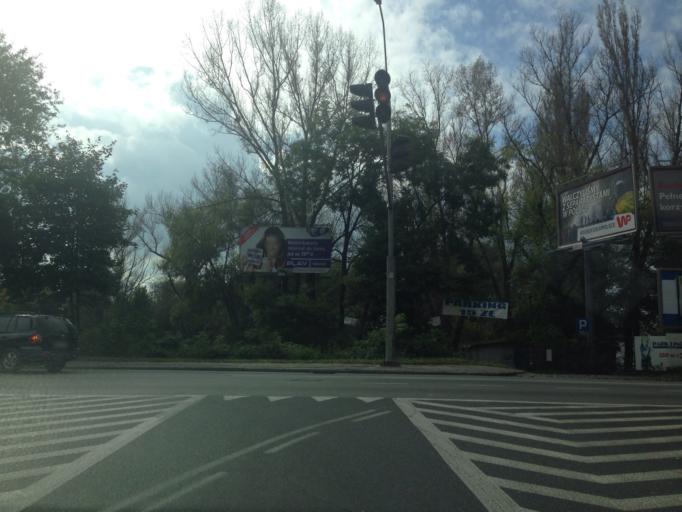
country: PL
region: Masovian Voivodeship
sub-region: Warszawa
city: Praga Polnoc
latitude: 52.2538
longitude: 21.0229
